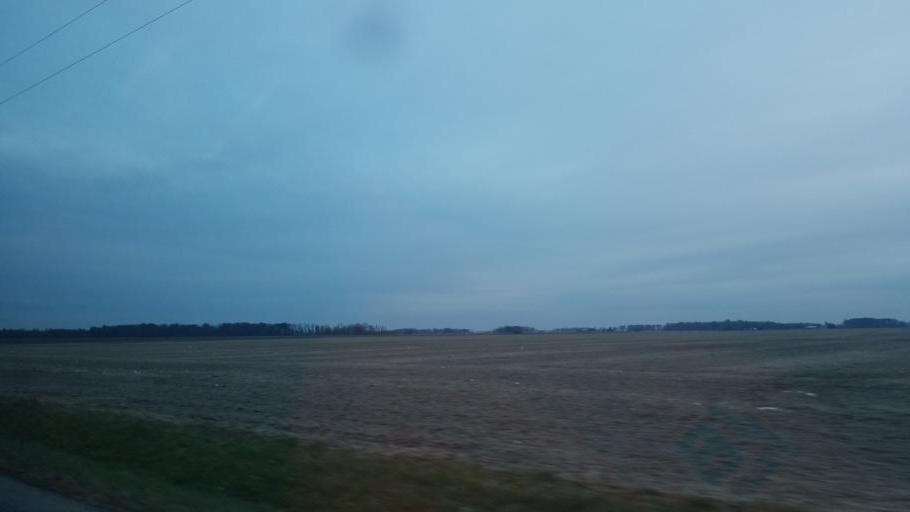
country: US
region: Indiana
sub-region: Adams County
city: Decatur
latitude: 40.7878
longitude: -84.9998
